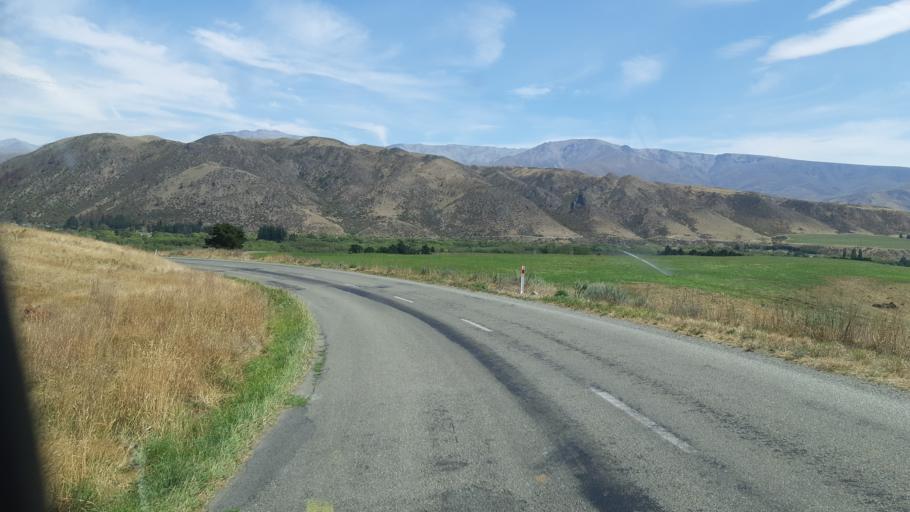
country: NZ
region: Otago
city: Oamaru
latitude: -44.7148
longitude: 170.4805
